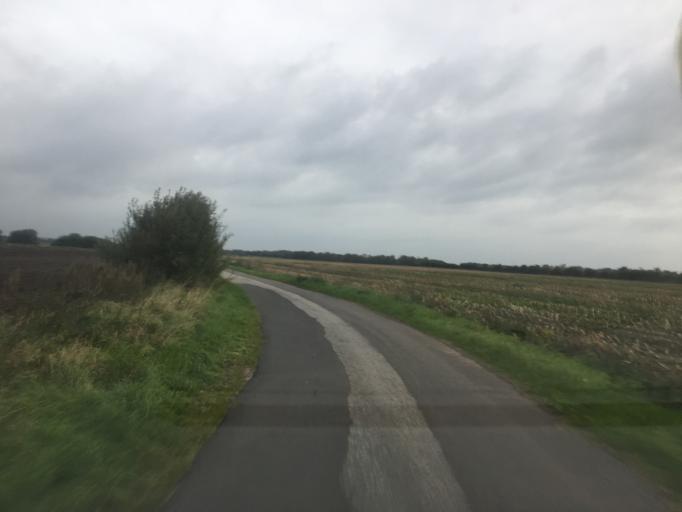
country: DK
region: South Denmark
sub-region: Tonder Kommune
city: Logumkloster
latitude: 54.9868
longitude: 9.0121
